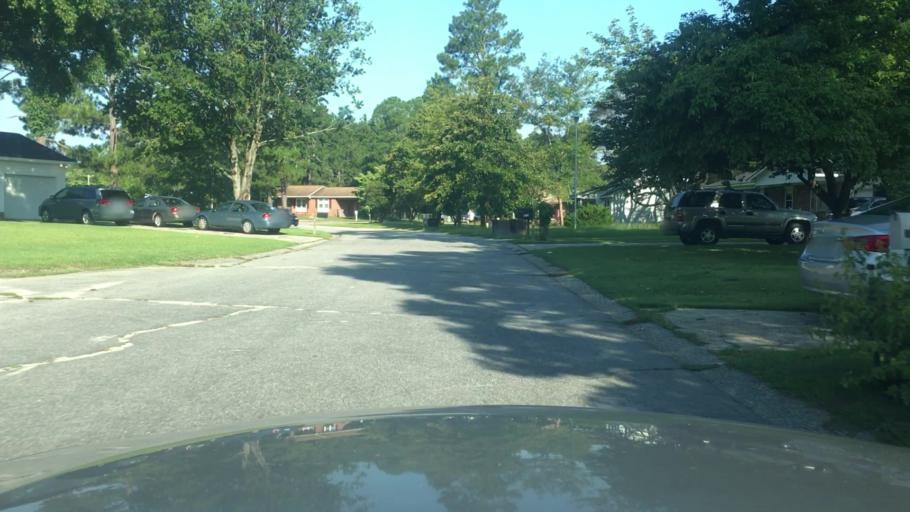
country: US
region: North Carolina
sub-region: Cumberland County
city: Spring Lake
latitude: 35.1586
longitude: -78.9079
